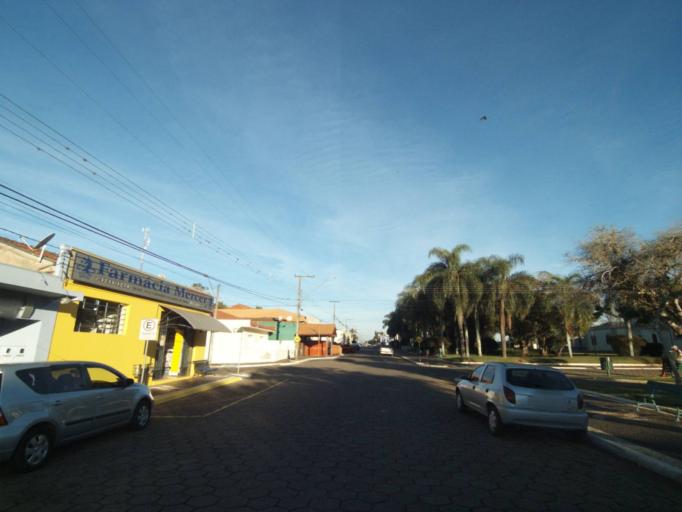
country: BR
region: Parana
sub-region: Tibagi
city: Tibagi
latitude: -24.5147
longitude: -50.4100
